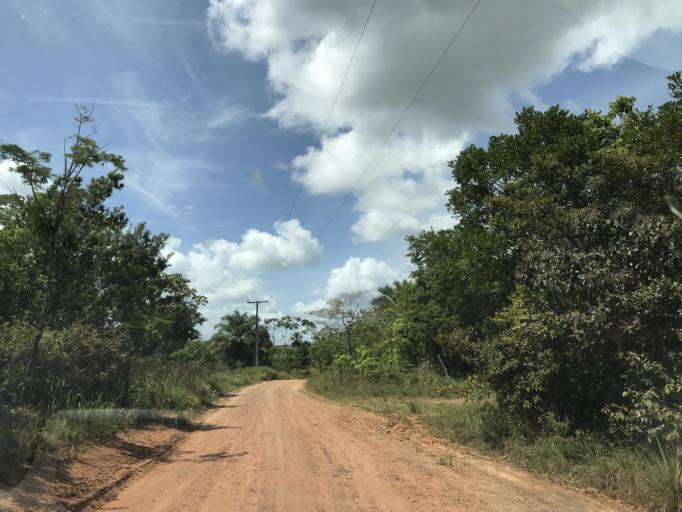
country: BR
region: Bahia
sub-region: Entre Rios
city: Entre Rios
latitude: -12.2210
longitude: -38.0849
